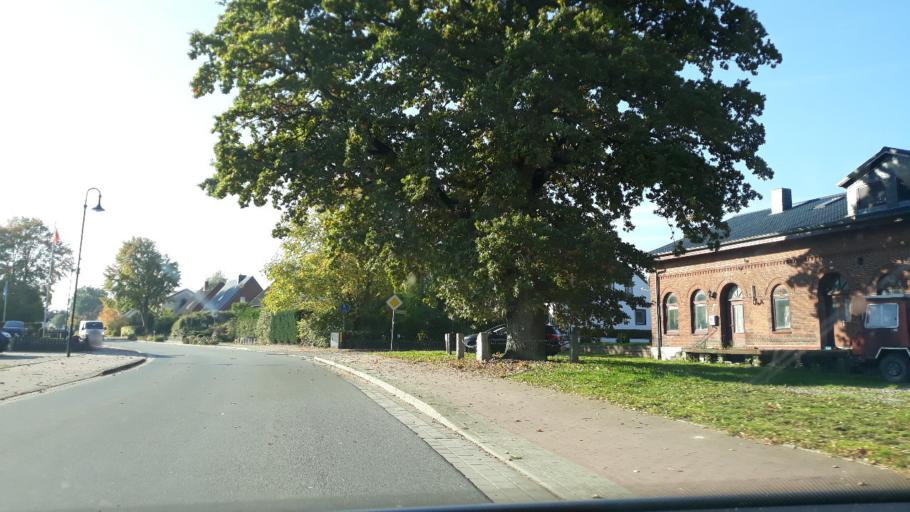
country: DE
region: Schleswig-Holstein
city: Boklund
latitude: 54.6067
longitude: 9.5841
